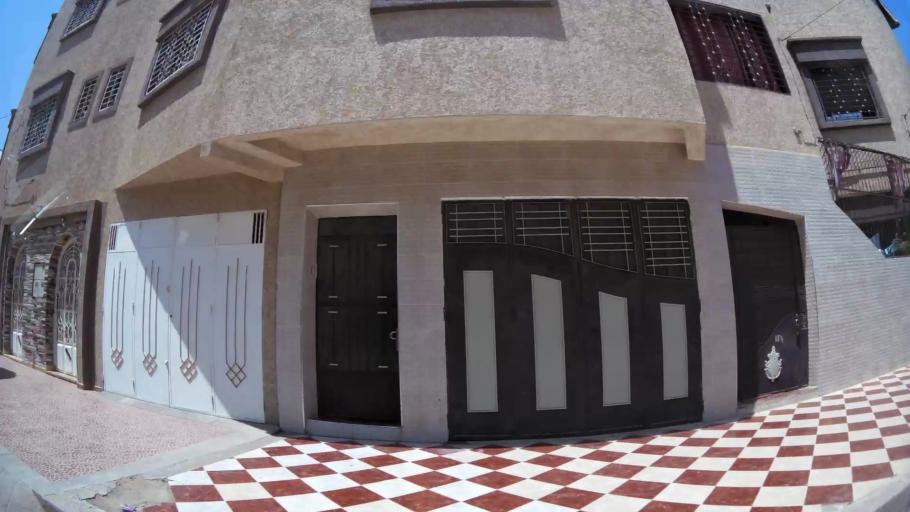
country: MA
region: Oriental
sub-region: Oujda-Angad
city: Oujda
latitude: 34.6843
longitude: -1.8977
